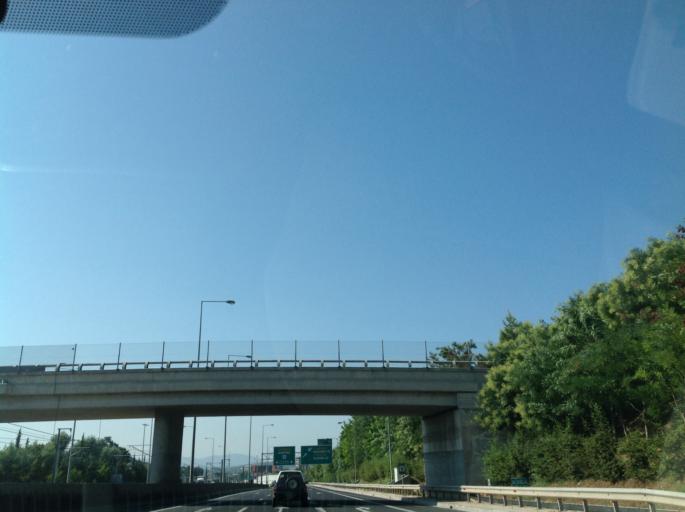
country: GR
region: Attica
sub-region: Nomarchia Anatolikis Attikis
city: Gerakas
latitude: 38.0115
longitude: 23.8679
